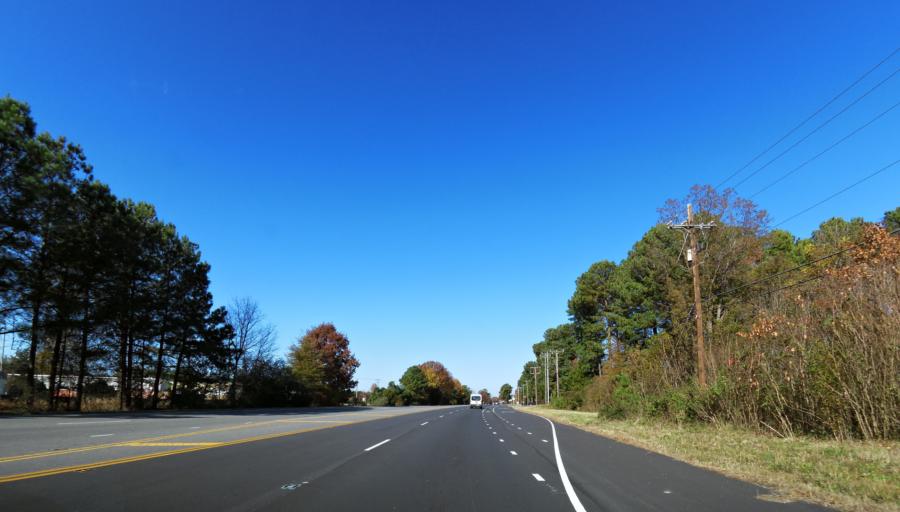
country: US
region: Virginia
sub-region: City of Williamsburg
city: Williamsburg
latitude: 37.2408
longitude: -76.6478
